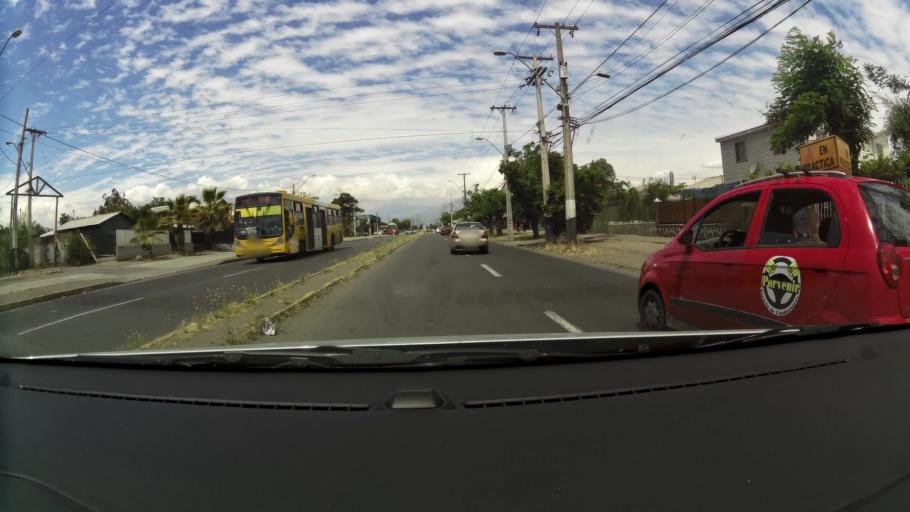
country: CL
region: Santiago Metropolitan
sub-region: Provincia de Santiago
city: La Pintana
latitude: -33.5739
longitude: -70.6594
